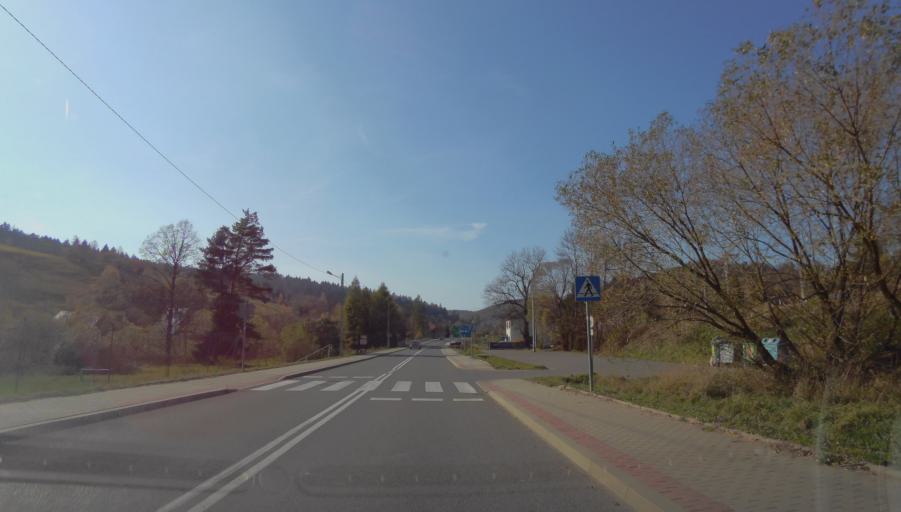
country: PL
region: Subcarpathian Voivodeship
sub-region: Powiat sanocki
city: Komancza
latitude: 49.3362
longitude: 22.0711
